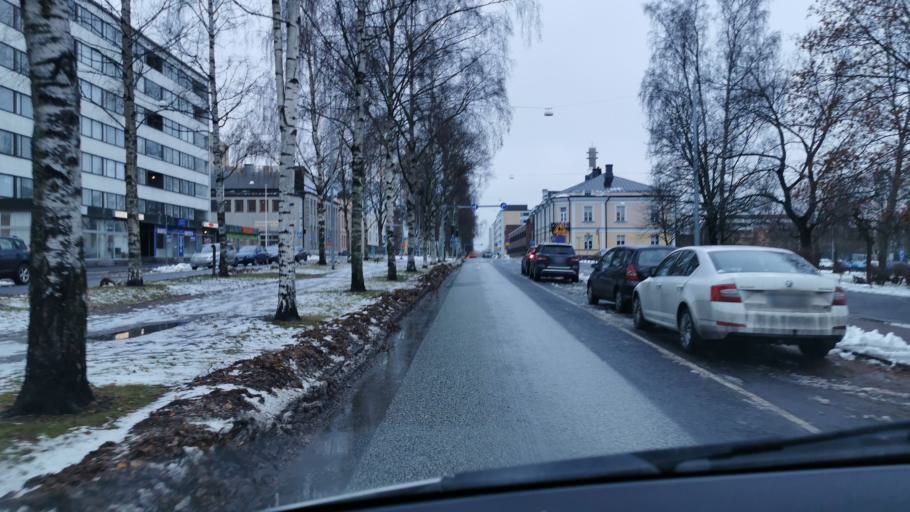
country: FI
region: Ostrobothnia
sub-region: Vaasa
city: Vaasa
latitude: 63.0961
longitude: 21.6090
